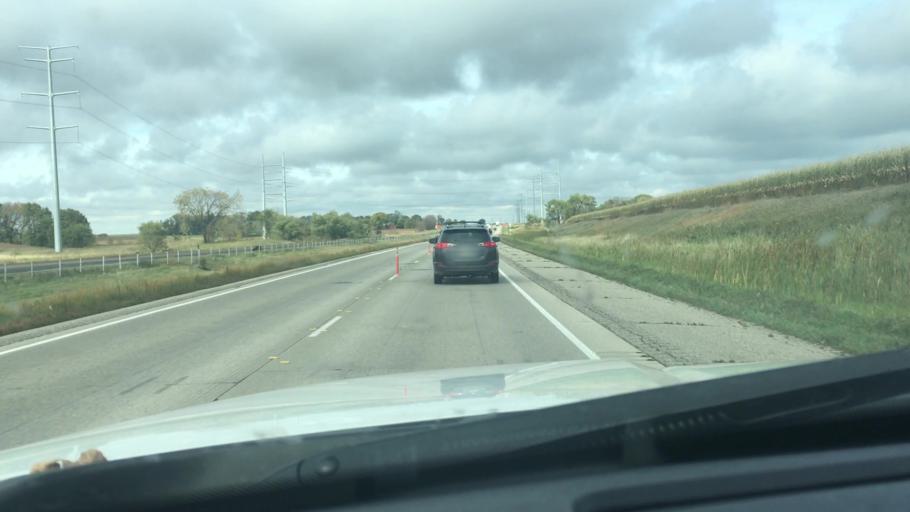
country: US
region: Minnesota
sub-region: Douglas County
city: Alexandria
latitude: 45.9166
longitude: -95.5529
